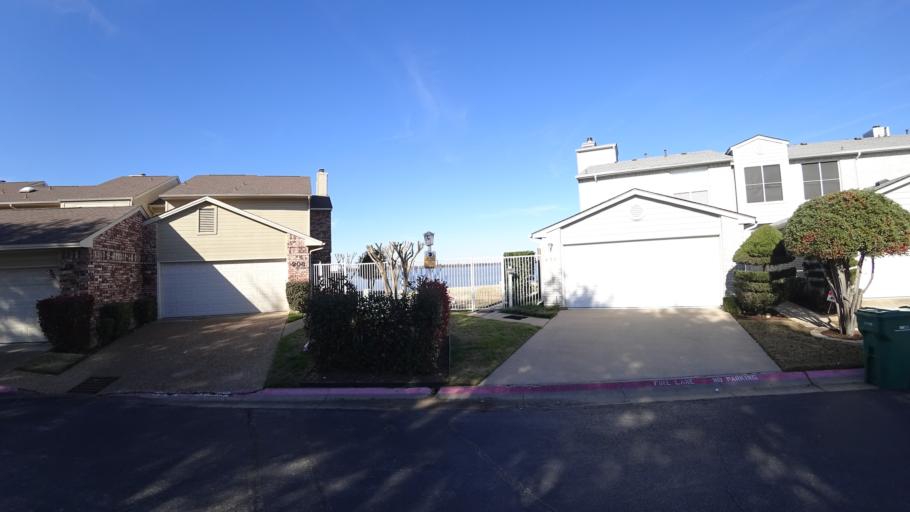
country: US
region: Texas
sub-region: Denton County
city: Highland Village
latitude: 33.0821
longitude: -97.0170
